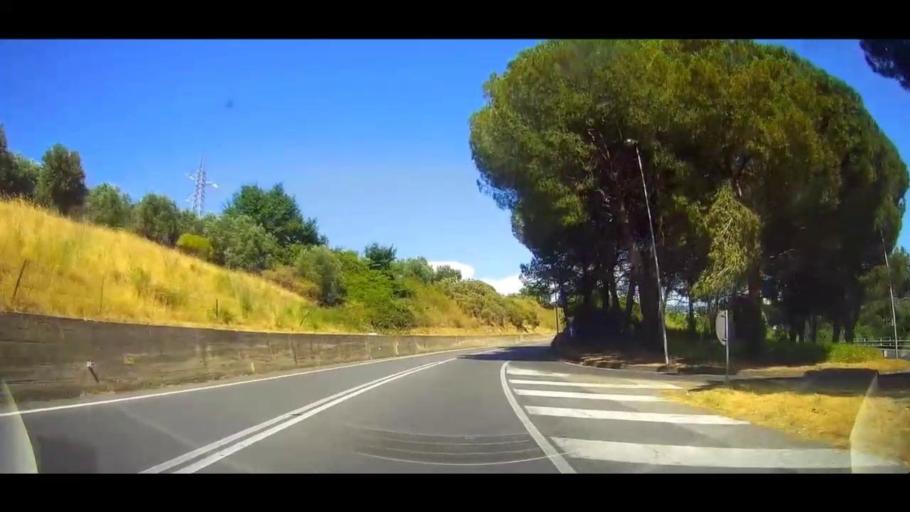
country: IT
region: Calabria
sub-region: Provincia di Cosenza
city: Cosenza
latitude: 39.2932
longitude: 16.2648
